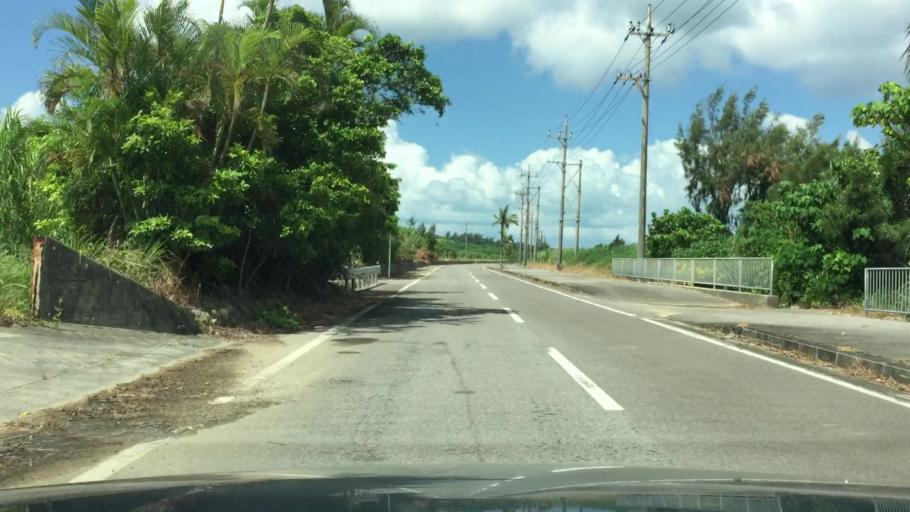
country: JP
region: Okinawa
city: Ishigaki
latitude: 24.3880
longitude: 124.1473
